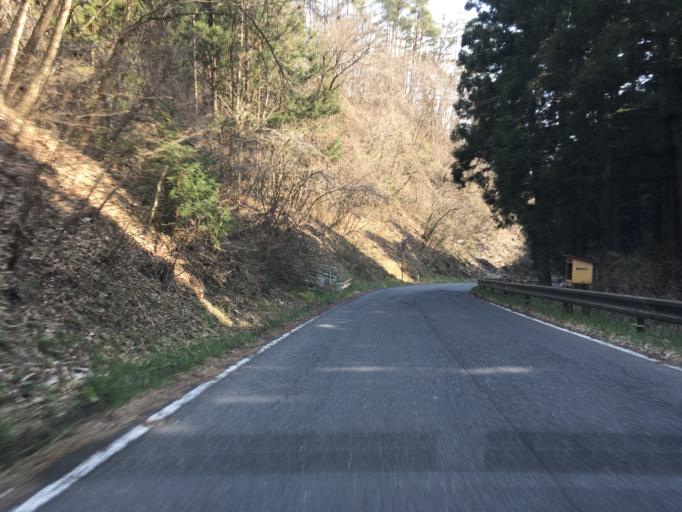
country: JP
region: Iwate
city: Ichinoseki
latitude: 38.8158
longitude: 141.3144
